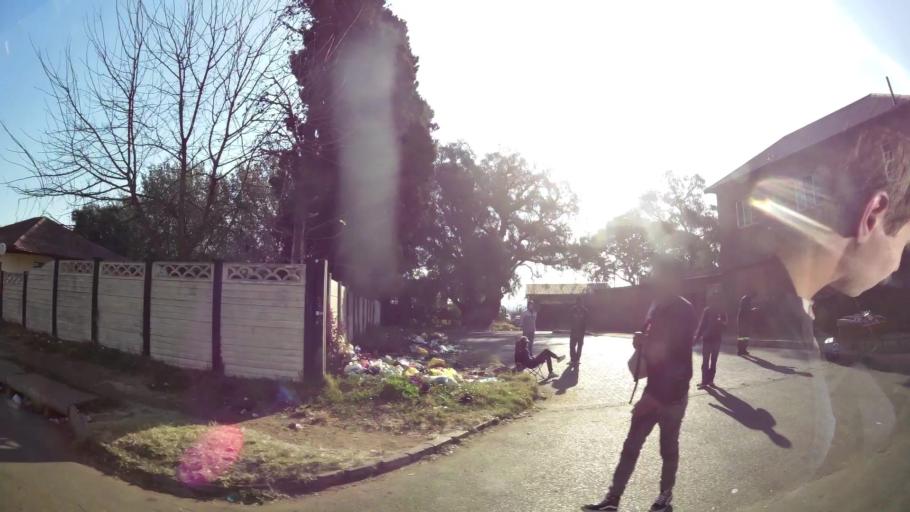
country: ZA
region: Gauteng
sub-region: West Rand District Municipality
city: Randfontein
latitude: -26.1835
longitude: 27.6975
